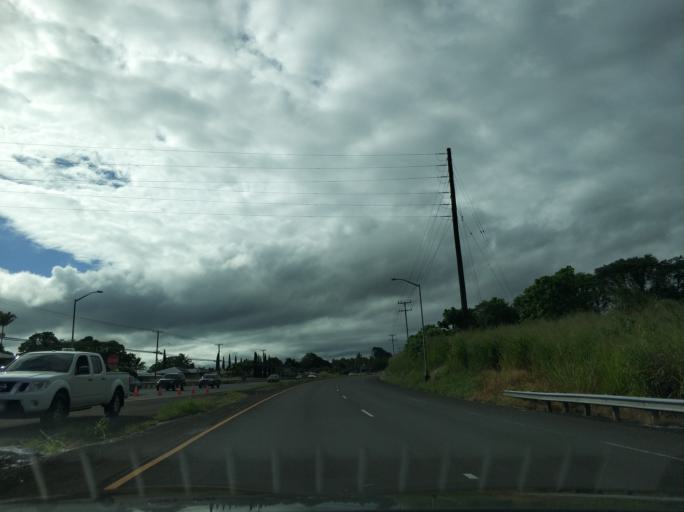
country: US
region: Hawaii
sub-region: Hawaii County
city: Kea'au
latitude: 19.6322
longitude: -155.0400
